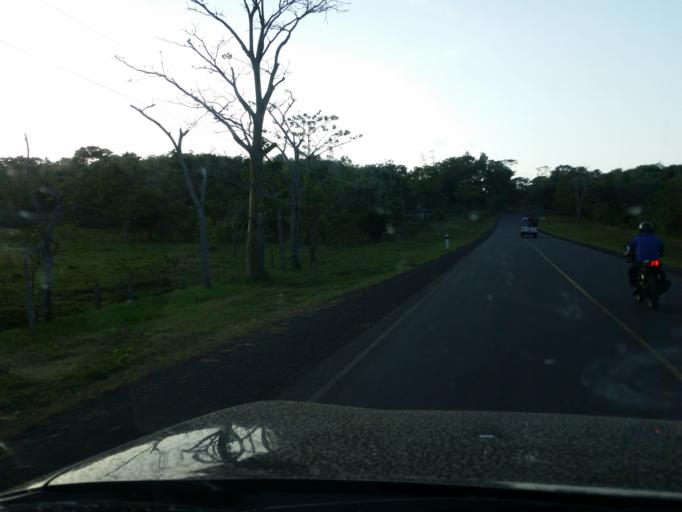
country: NI
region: Rio San Juan
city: San Carlos
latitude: 11.2487
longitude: -84.7000
